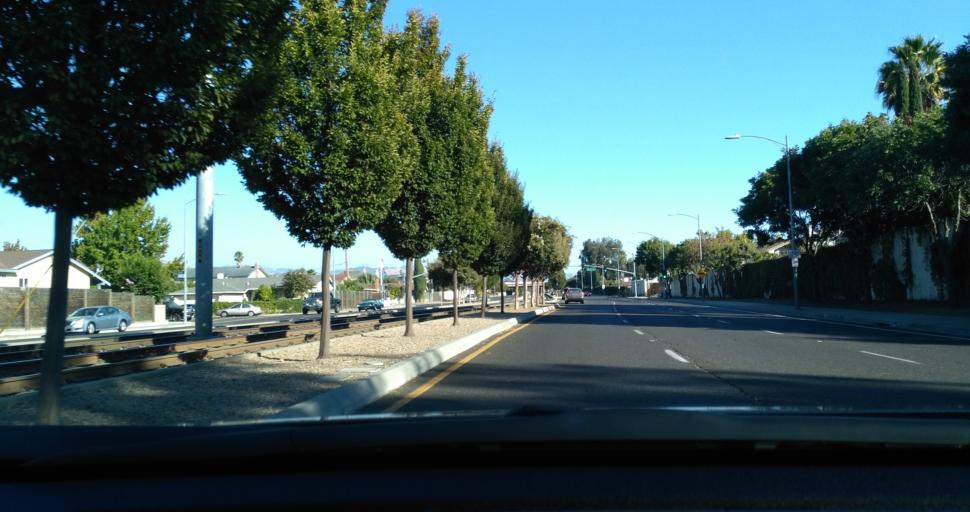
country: US
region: California
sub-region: Santa Clara County
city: Milpitas
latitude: 37.4023
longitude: -121.8807
